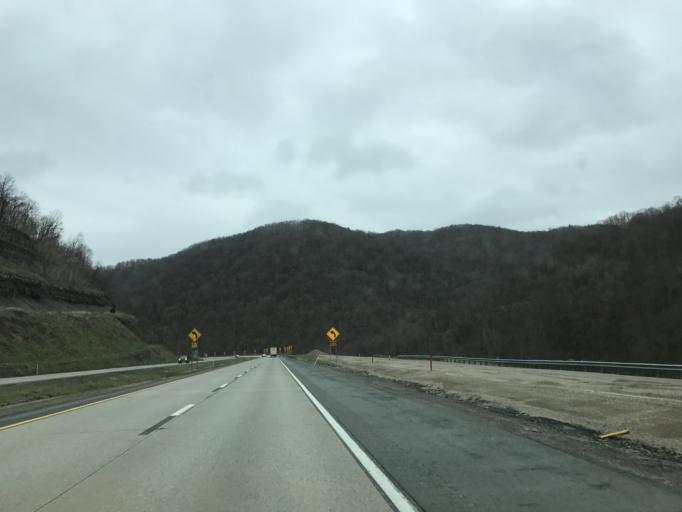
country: US
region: West Virginia
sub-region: Summers County
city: Hinton
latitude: 37.7798
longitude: -80.9344
